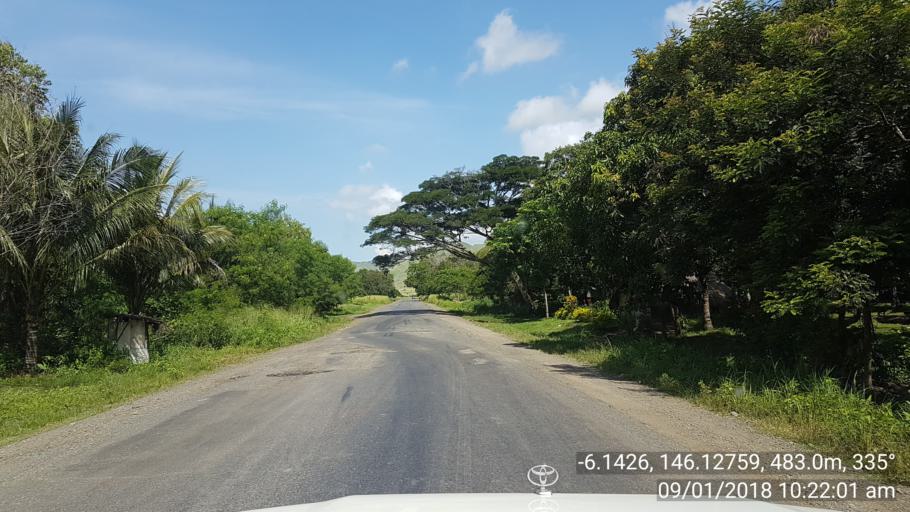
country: PG
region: Eastern Highlands
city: Kainantu
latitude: -6.1425
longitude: 146.1275
